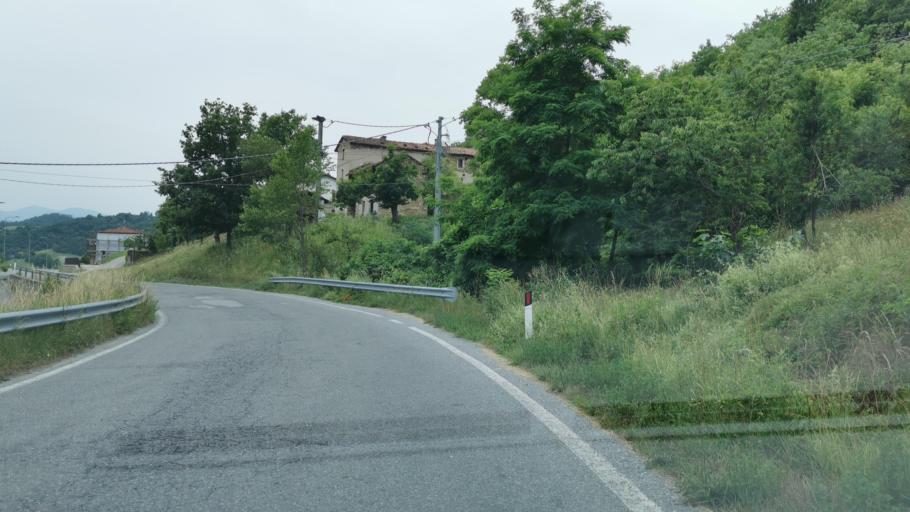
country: IT
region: Piedmont
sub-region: Provincia di Cuneo
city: Torresina
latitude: 44.4221
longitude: 8.0529
